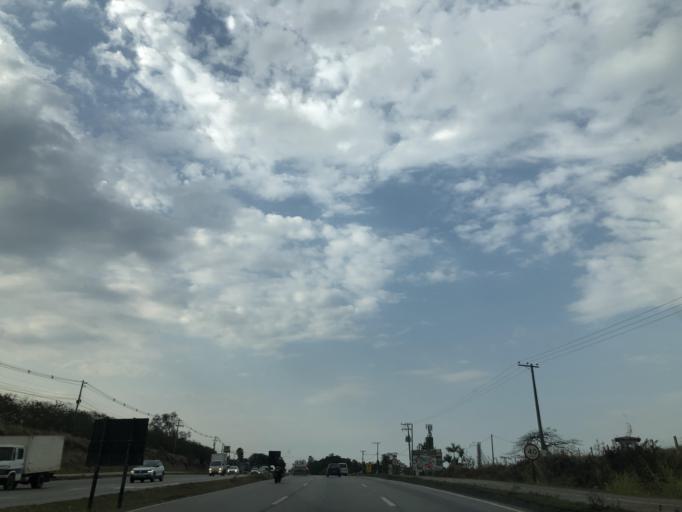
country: BR
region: Sao Paulo
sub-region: Votorantim
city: Votorantim
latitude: -23.5546
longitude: -47.4862
